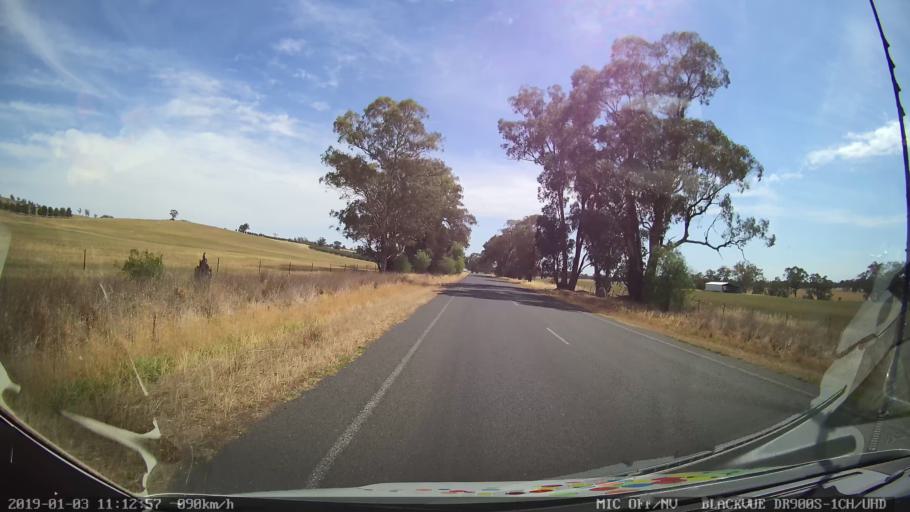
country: AU
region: New South Wales
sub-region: Young
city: Young
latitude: -34.1950
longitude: 148.2617
